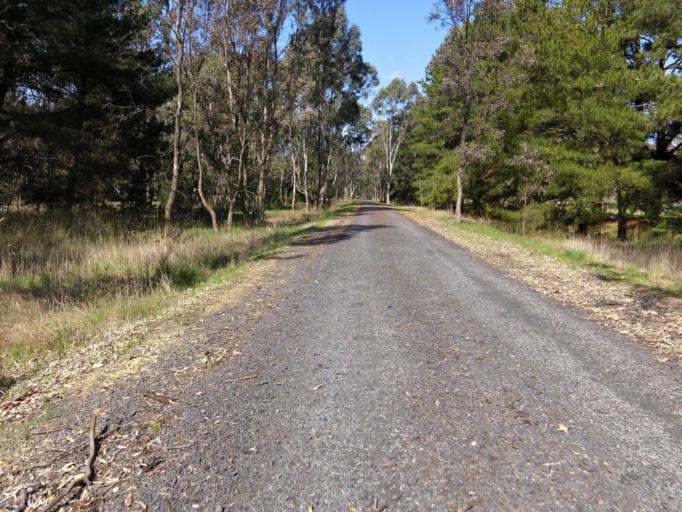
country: AU
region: Victoria
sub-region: Murrindindi
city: Alexandra
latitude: -36.9864
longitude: 145.7316
